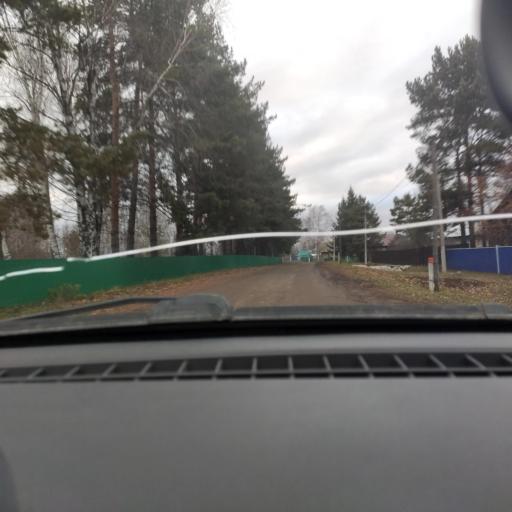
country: RU
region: Bashkortostan
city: Ulukulevo
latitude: 54.4449
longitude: 56.4603
